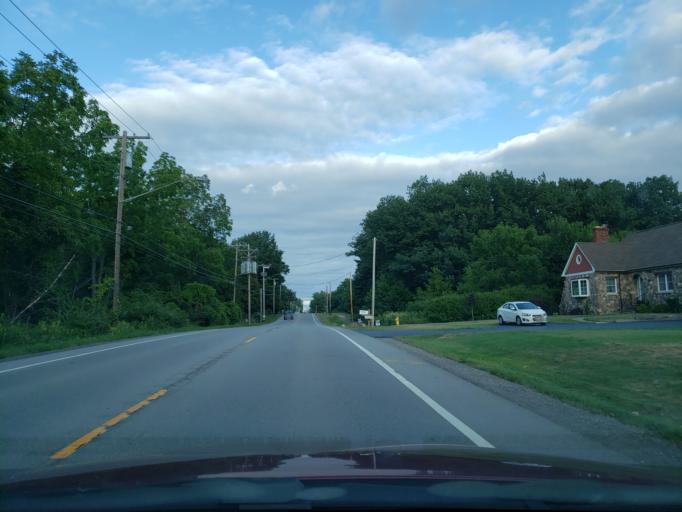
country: US
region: New York
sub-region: Monroe County
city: Greece
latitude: 43.2535
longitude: -77.7279
